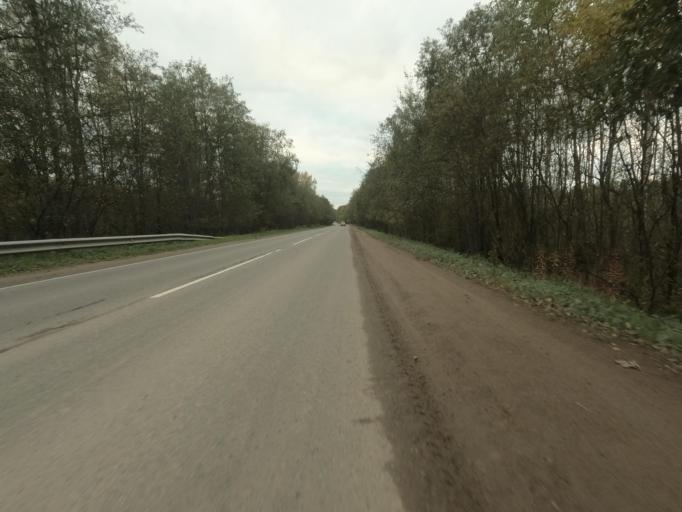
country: RU
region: Leningrad
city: Pavlovo
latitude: 59.7936
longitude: 30.9554
